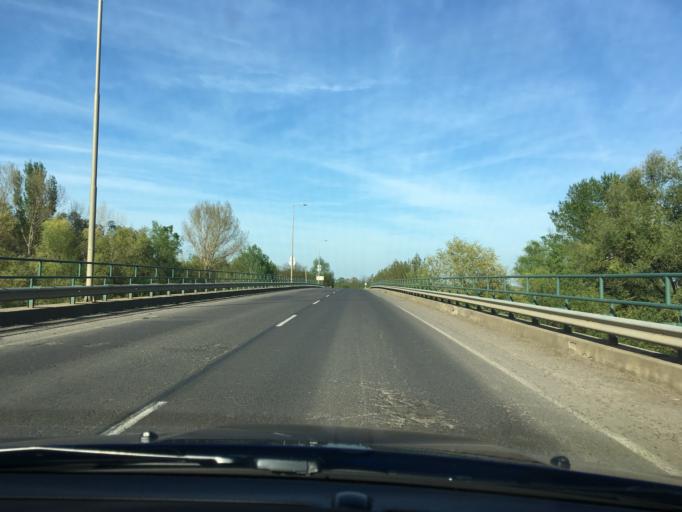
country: HU
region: Bekes
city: Korostarcsa
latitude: 46.8834
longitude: 21.0313
